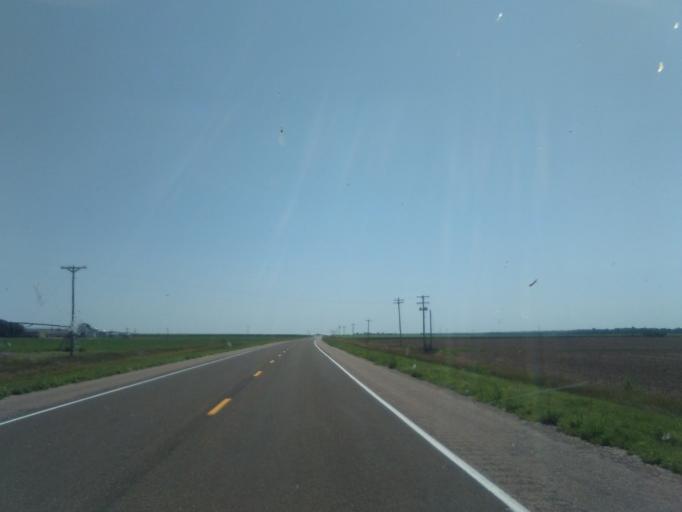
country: US
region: Nebraska
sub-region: Dundy County
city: Benkelman
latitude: 40.1257
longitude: -101.3495
